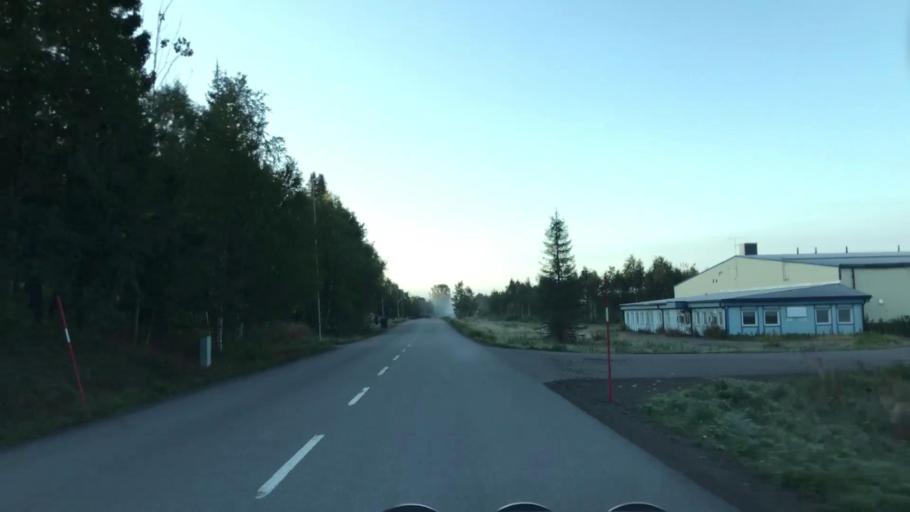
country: SE
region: Norrbotten
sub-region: Gallivare Kommun
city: Malmberget
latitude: 67.6508
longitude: 21.0431
